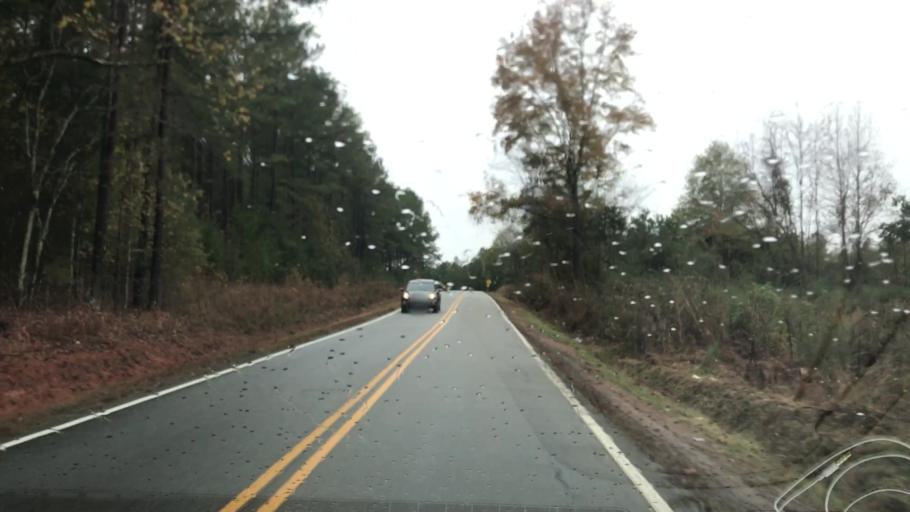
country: US
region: South Carolina
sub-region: Greenwood County
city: Ninety Six
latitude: 34.3082
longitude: -81.9757
